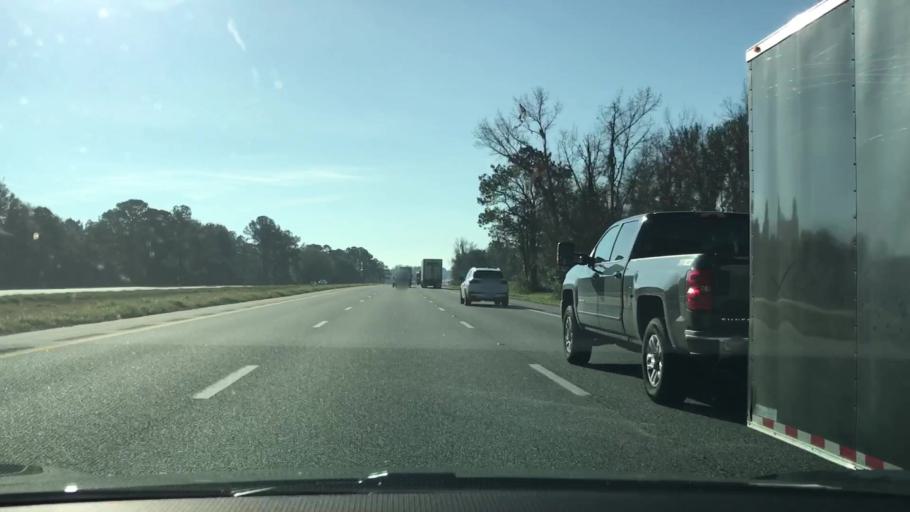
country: US
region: Florida
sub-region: Hamilton County
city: Jasper
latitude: 30.5446
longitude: -83.0690
